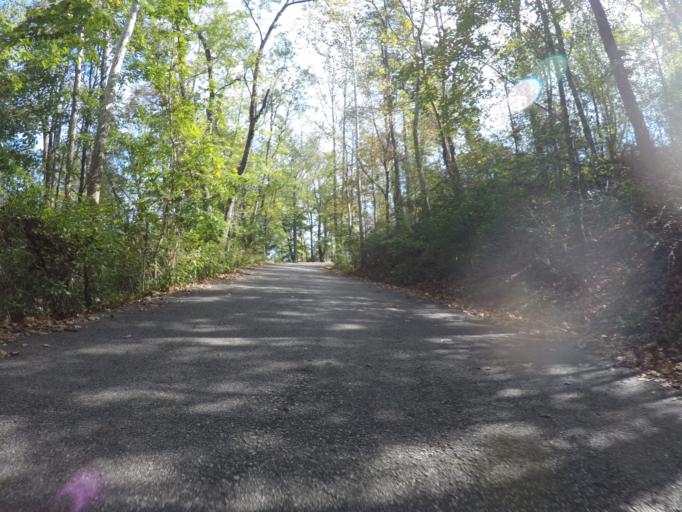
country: US
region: West Virginia
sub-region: Cabell County
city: Huntington
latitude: 38.3944
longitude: -82.3883
